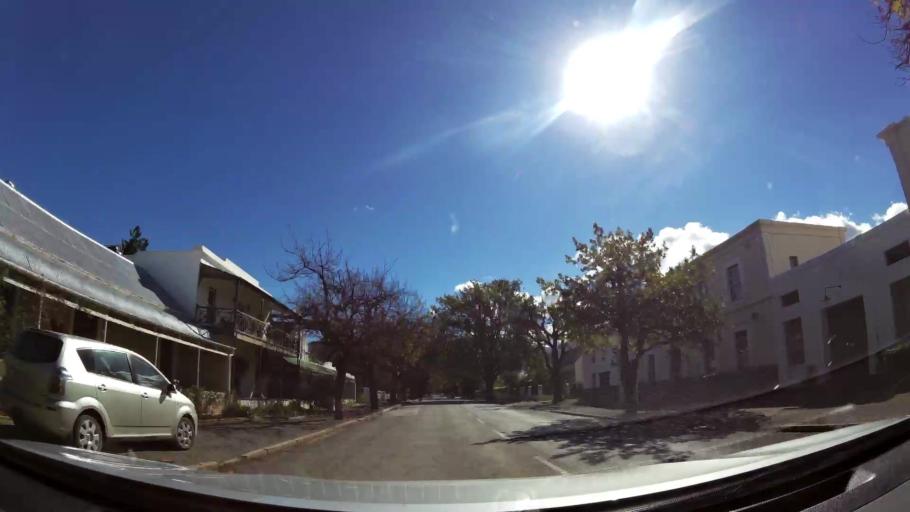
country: ZA
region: Western Cape
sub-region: Cape Winelands District Municipality
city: Ashton
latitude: -33.8000
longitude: 19.8810
